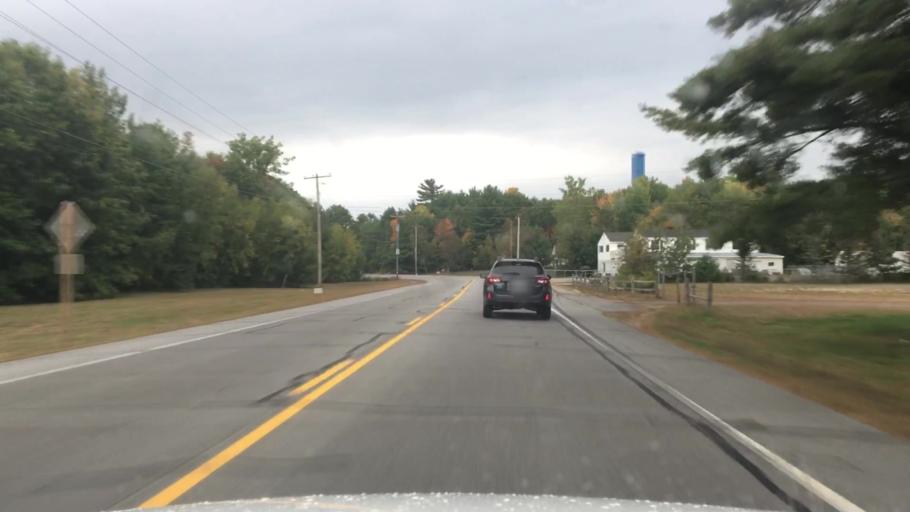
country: US
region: Maine
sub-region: York County
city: Waterboro
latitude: 43.5232
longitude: -70.7193
